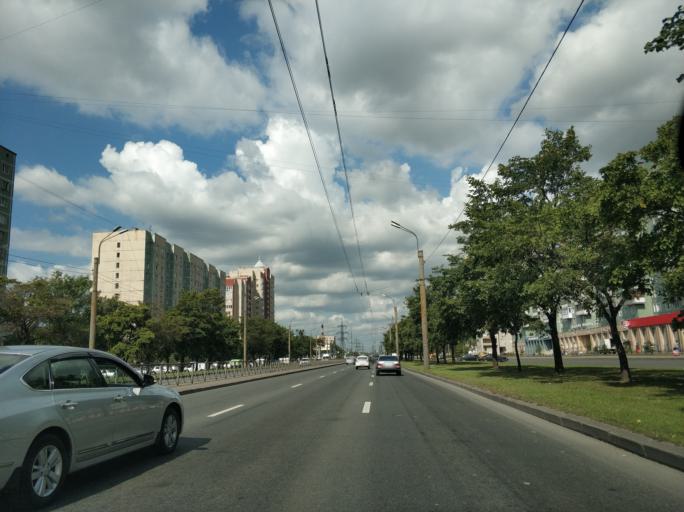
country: RU
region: St.-Petersburg
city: Krasnogvargeisky
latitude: 59.9529
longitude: 30.4702
